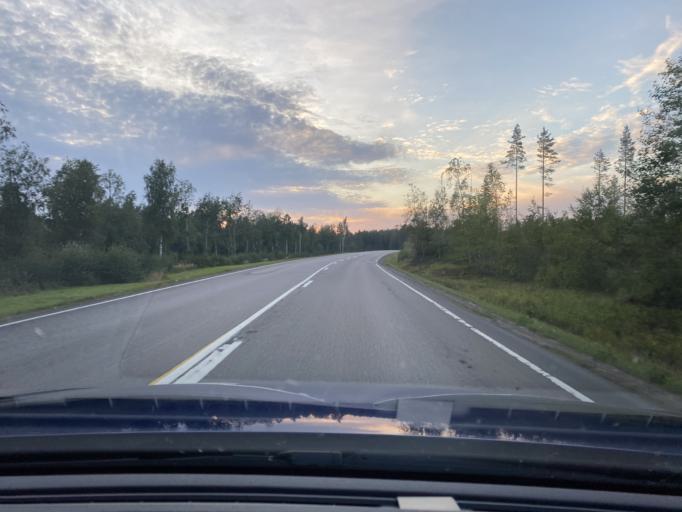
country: FI
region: Satakunta
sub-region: Pohjois-Satakunta
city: Honkajoki
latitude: 61.9406
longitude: 22.2362
